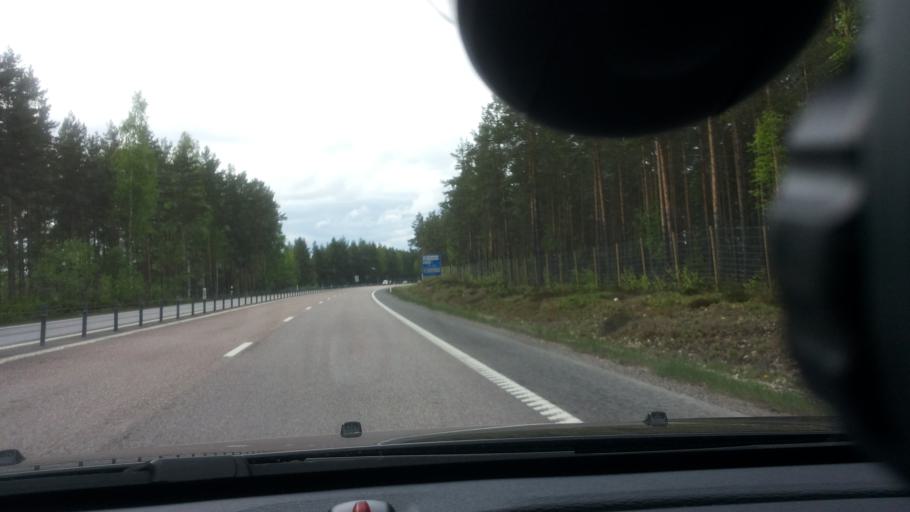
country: SE
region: Gaevleborg
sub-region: Gavle Kommun
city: Norrsundet
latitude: 60.9945
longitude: 16.9986
